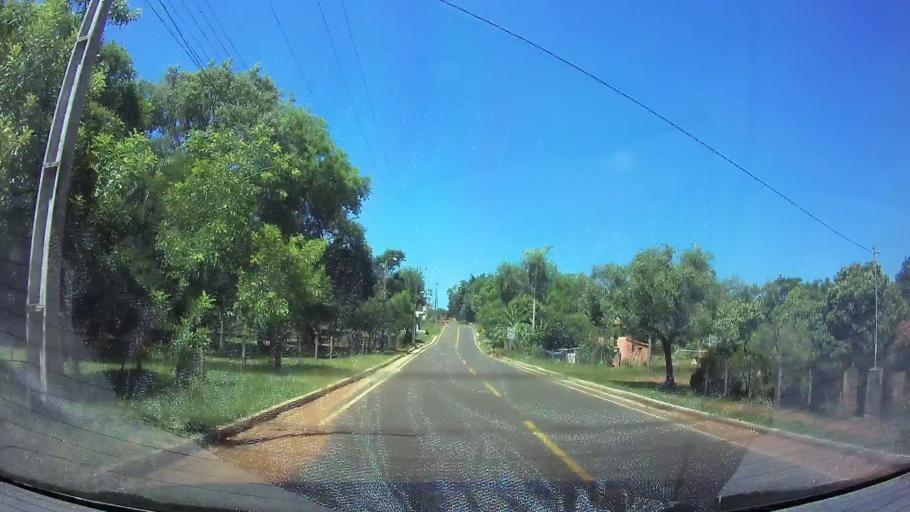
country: PY
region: Central
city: Aregua
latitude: -25.2566
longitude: -57.4471
